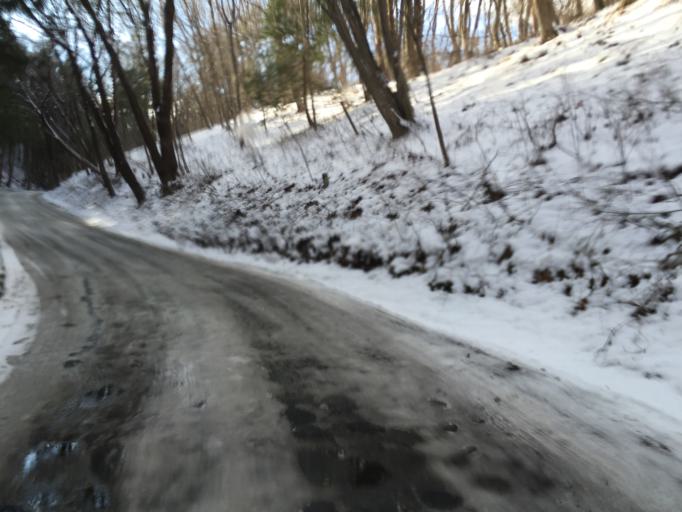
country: JP
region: Fukushima
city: Nihommatsu
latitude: 37.6821
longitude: 140.3458
